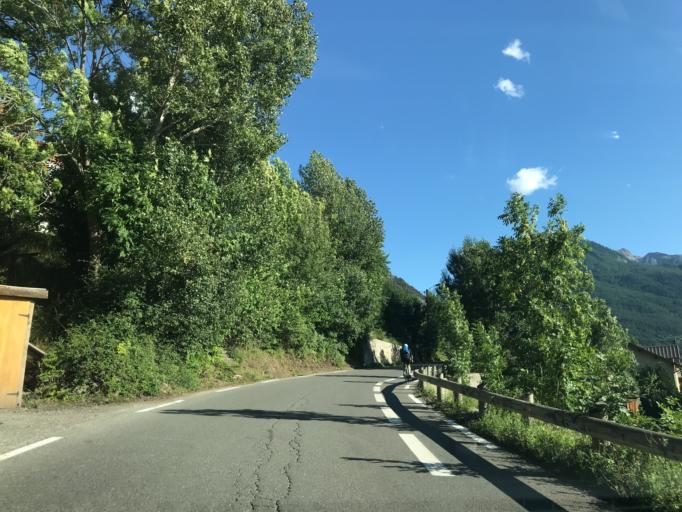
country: FR
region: Provence-Alpes-Cote d'Azur
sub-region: Departement des Hautes-Alpes
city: Briancon
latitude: 44.8907
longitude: 6.6387
